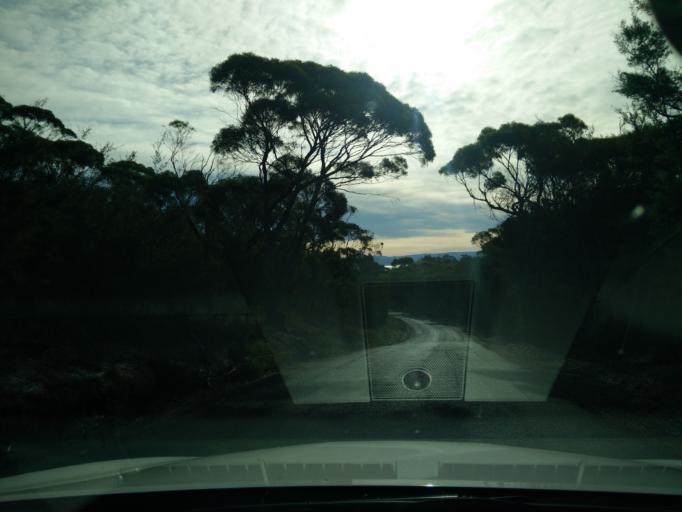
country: AU
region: Tasmania
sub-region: Break O'Day
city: St Helens
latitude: -42.1361
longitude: 148.3082
